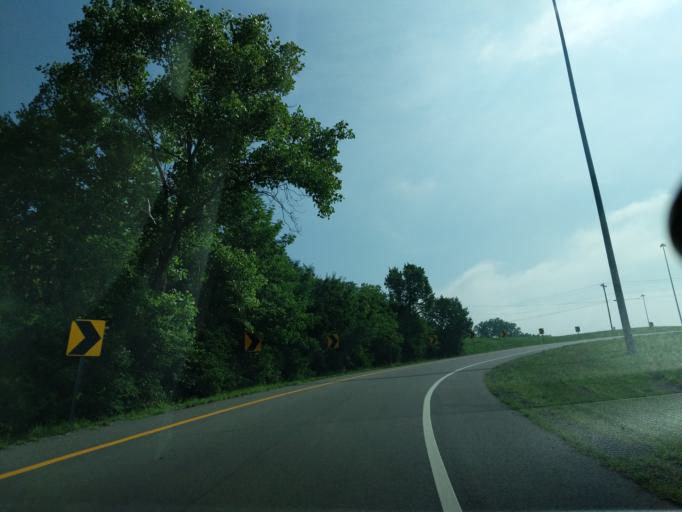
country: US
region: Tennessee
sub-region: Davidson County
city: Goodlettsville
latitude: 36.3083
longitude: -86.6976
